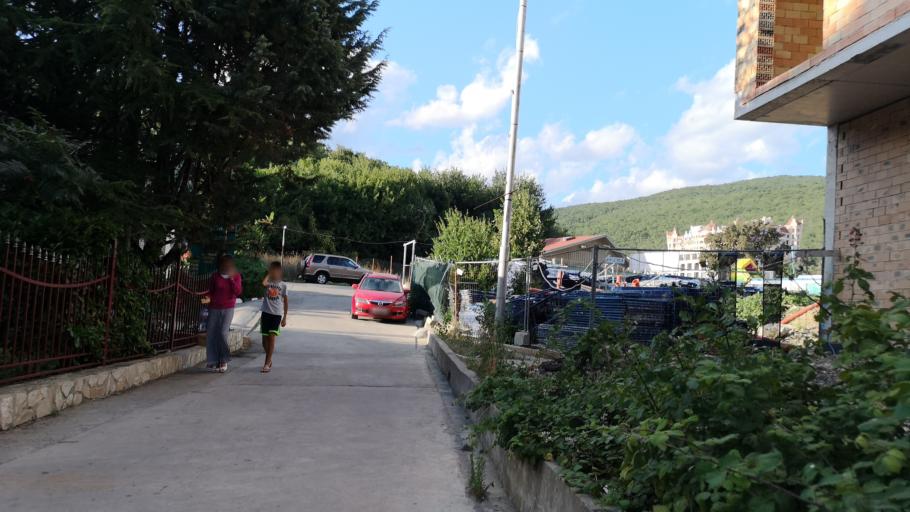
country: BG
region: Burgas
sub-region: Obshtina Nesebur
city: Sveti Vlas
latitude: 42.7035
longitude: 27.8083
